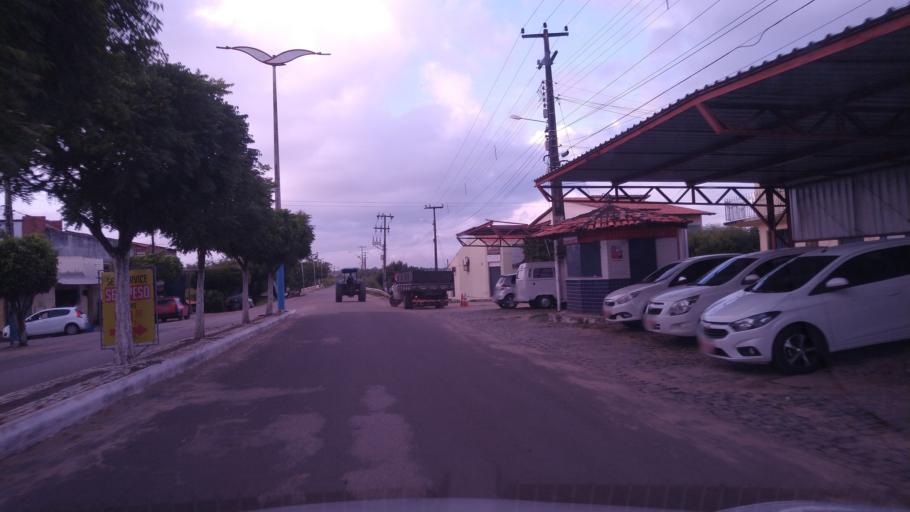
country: BR
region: Ceara
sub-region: Chorozinho
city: Chorozinho
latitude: -4.3026
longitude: -38.4976
